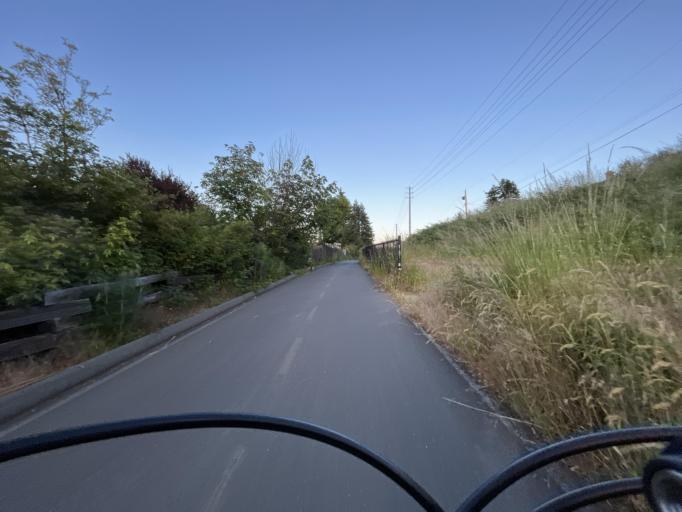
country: CA
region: British Columbia
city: Victoria
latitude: 48.4380
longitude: -123.4058
